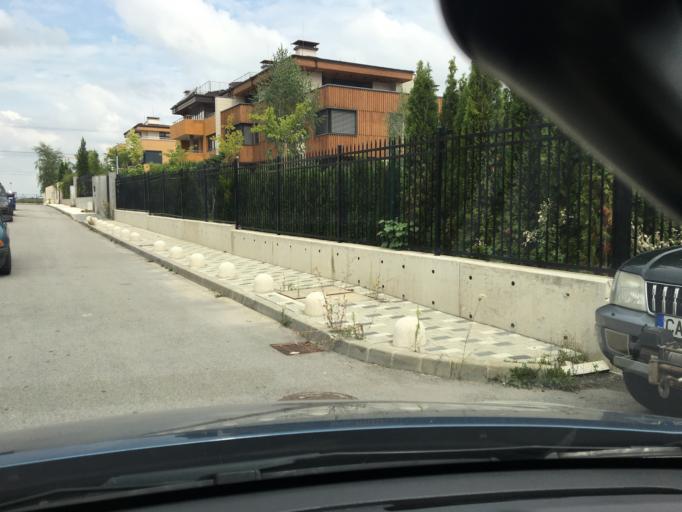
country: BG
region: Sofia-Capital
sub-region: Stolichna Obshtina
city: Sofia
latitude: 42.6159
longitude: 23.3669
